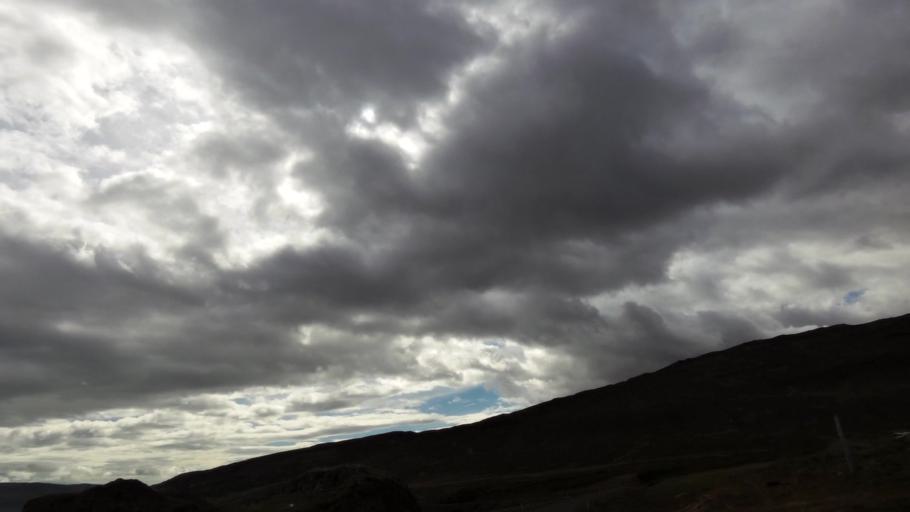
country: IS
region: West
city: Stykkisholmur
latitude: 65.5906
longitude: -22.1389
